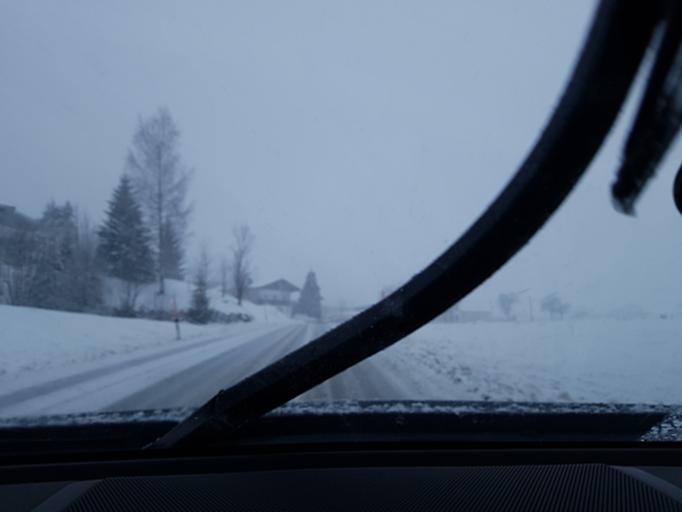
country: AT
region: Salzburg
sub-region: Politischer Bezirk Hallein
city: Abtenau
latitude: 47.5612
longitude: 13.3787
